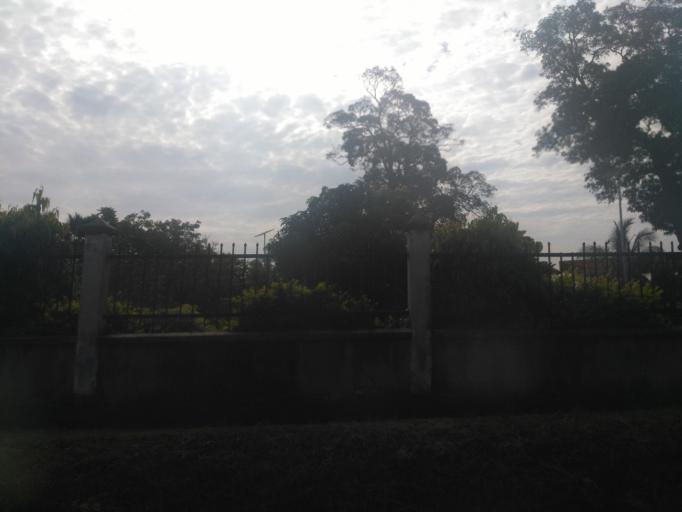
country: TZ
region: Zanzibar Urban/West
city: Zanzibar
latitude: -6.1649
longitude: 39.2048
